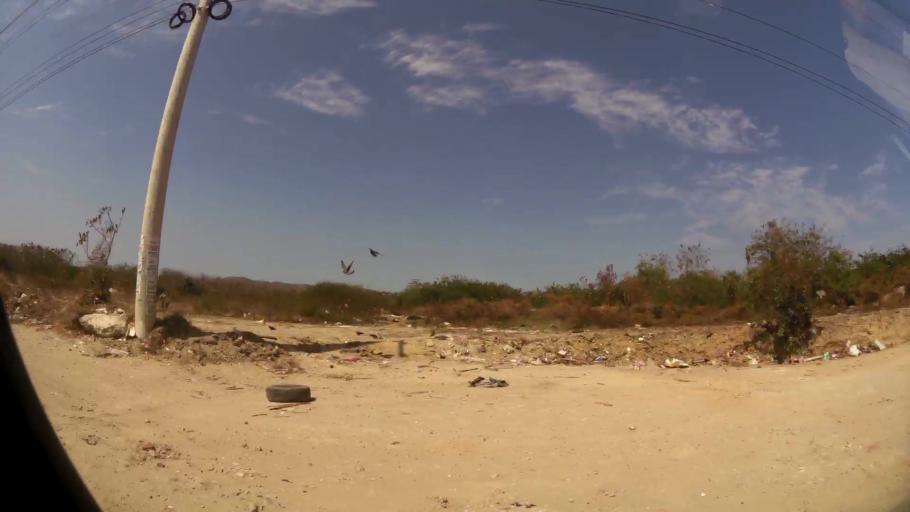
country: CO
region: Atlantico
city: Barranquilla
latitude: 10.9823
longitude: -74.8377
